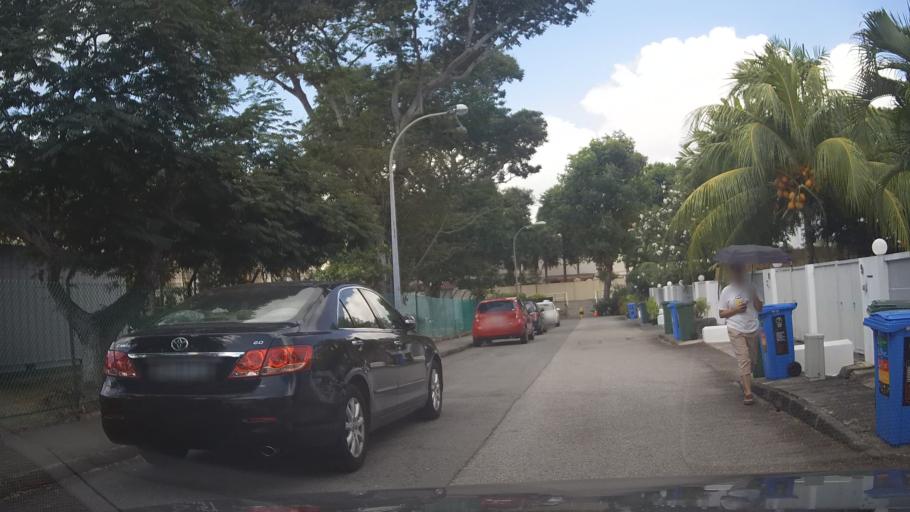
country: SG
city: Singapore
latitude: 1.3120
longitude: 103.9290
